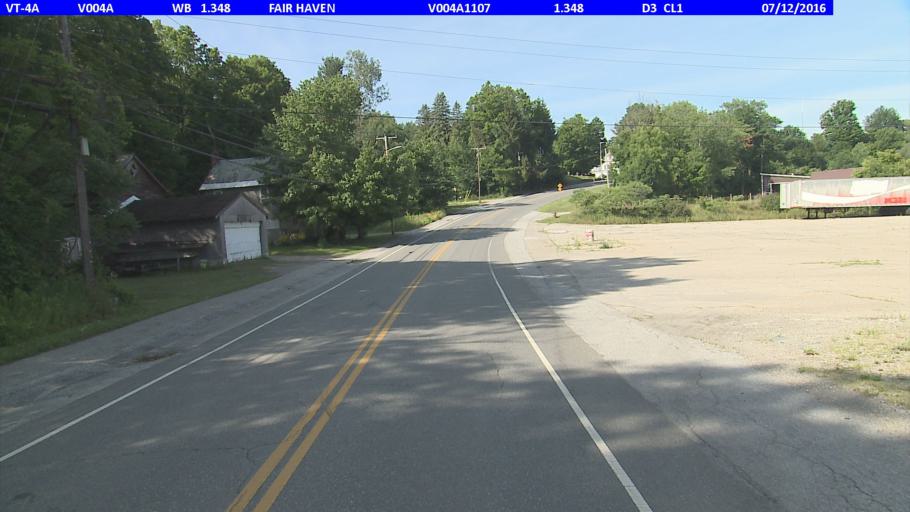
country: US
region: Vermont
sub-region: Rutland County
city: Fair Haven
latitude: 43.5887
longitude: -73.2673
